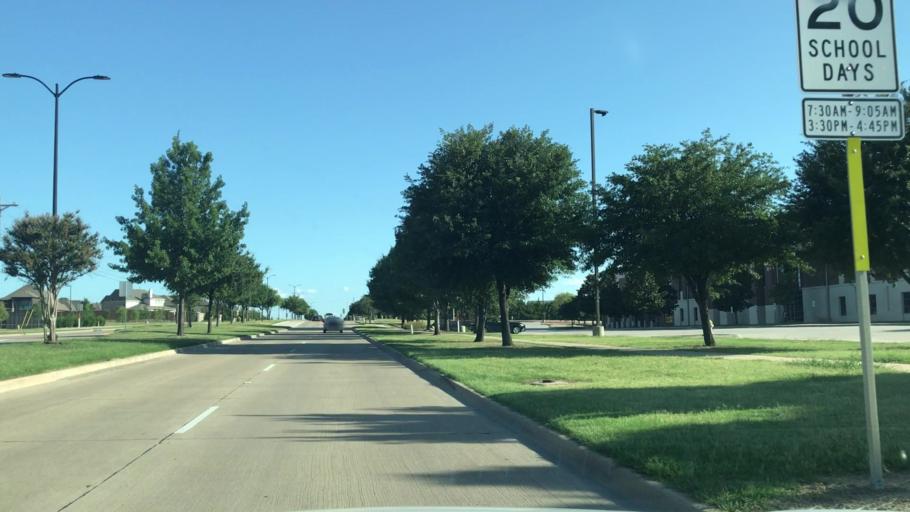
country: US
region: Texas
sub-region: Collin County
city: Frisco
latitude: 33.1372
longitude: -96.7682
